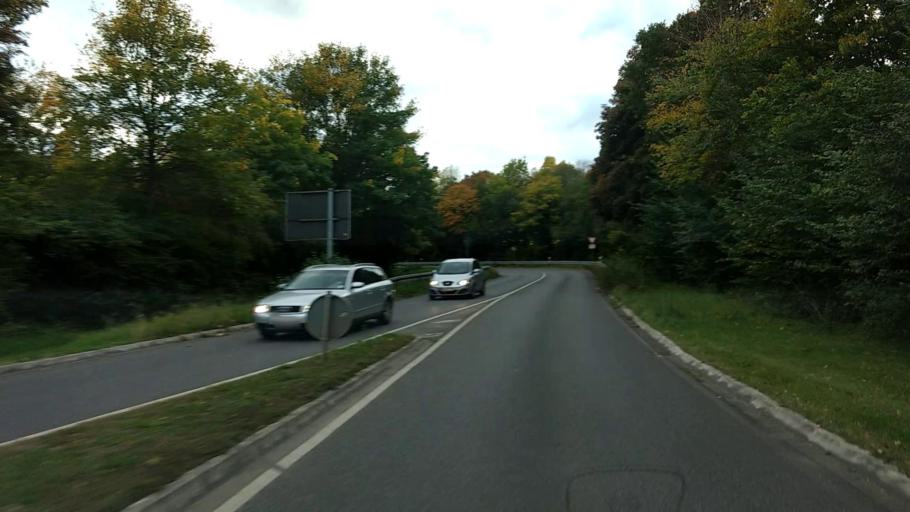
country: DE
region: North Rhine-Westphalia
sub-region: Regierungsbezirk Koln
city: Kerpen
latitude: 50.9248
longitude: 6.7052
